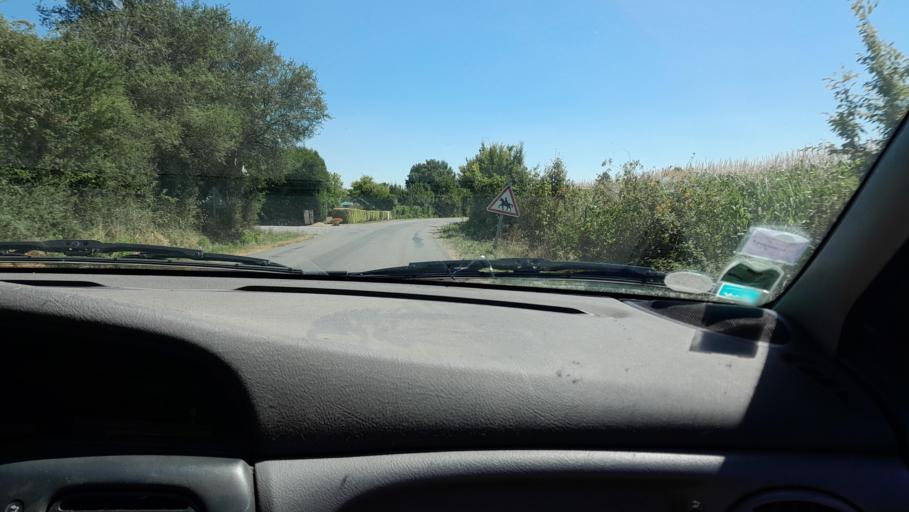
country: FR
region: Pays de la Loire
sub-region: Departement de Maine-et-Loire
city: Pouance
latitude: 47.8040
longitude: -1.2027
